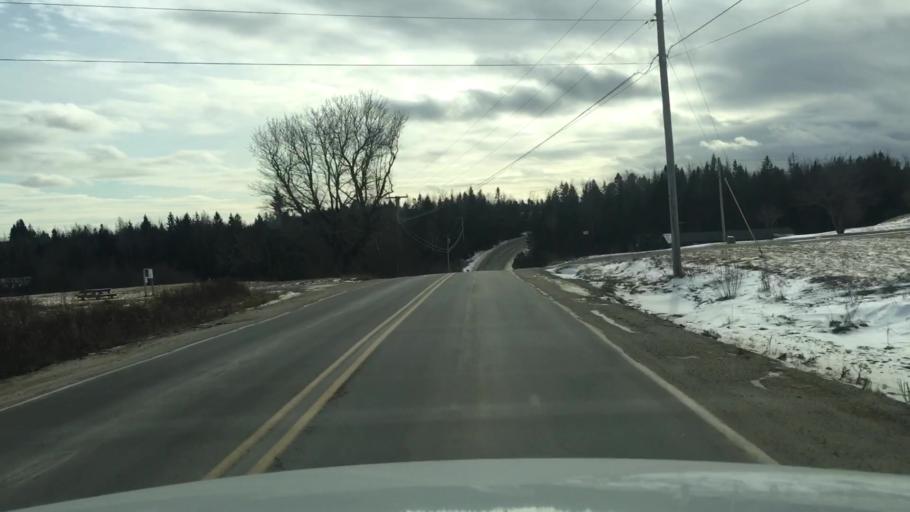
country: US
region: Maine
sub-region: Washington County
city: Jonesport
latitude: 44.6301
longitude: -67.5961
